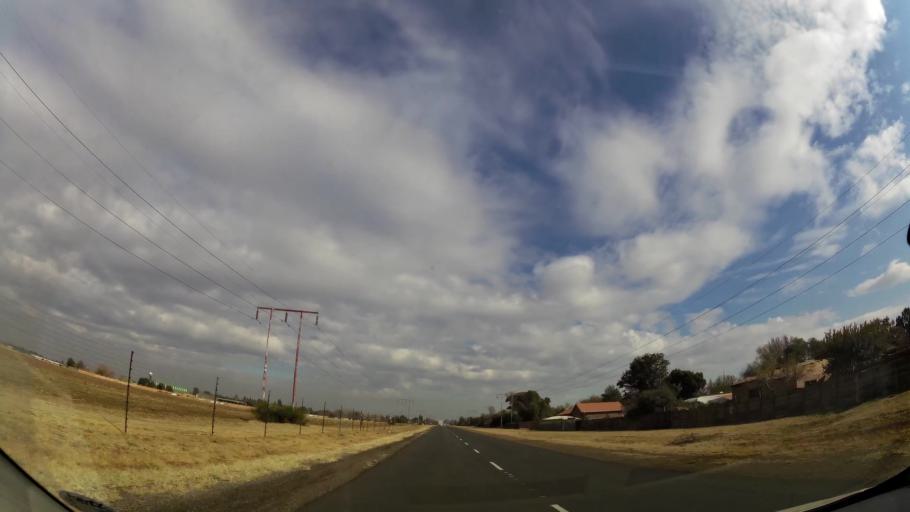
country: ZA
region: Gauteng
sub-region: Sedibeng District Municipality
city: Meyerton
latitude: -26.5570
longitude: 28.0392
